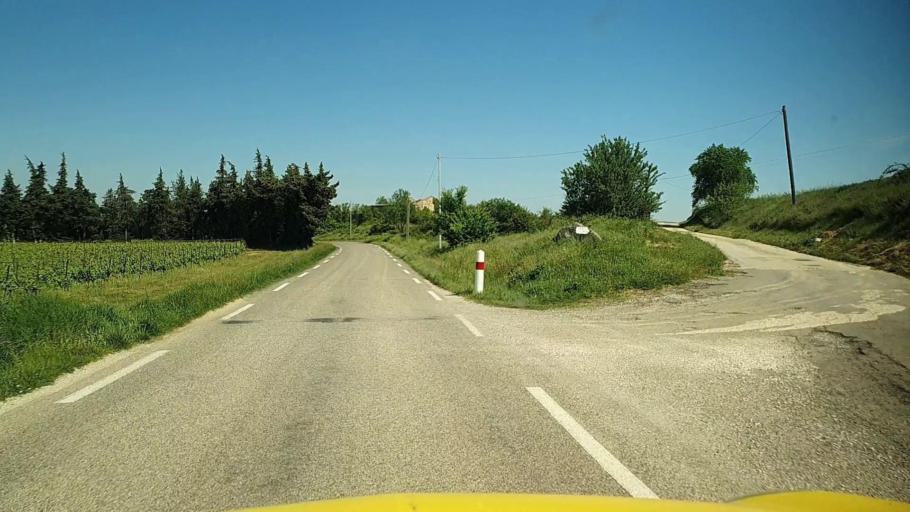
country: FR
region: Languedoc-Roussillon
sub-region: Departement du Gard
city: Saint-Chaptes
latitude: 43.9514
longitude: 4.3050
